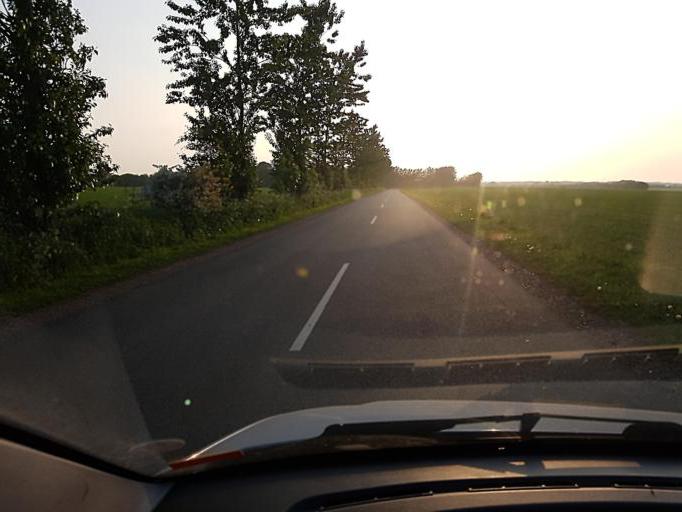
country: DK
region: South Denmark
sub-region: Esbjerg Kommune
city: Tjaereborg
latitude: 55.5475
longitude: 8.5618
